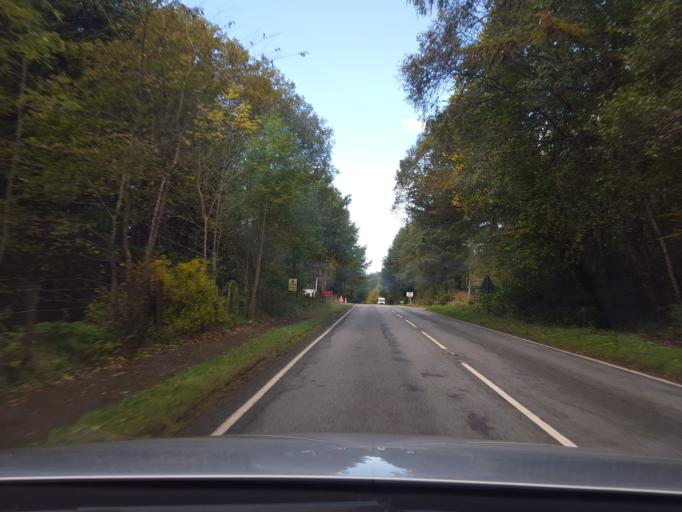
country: GB
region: Scotland
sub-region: Highland
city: Fort William
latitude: 57.2383
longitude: -5.4416
